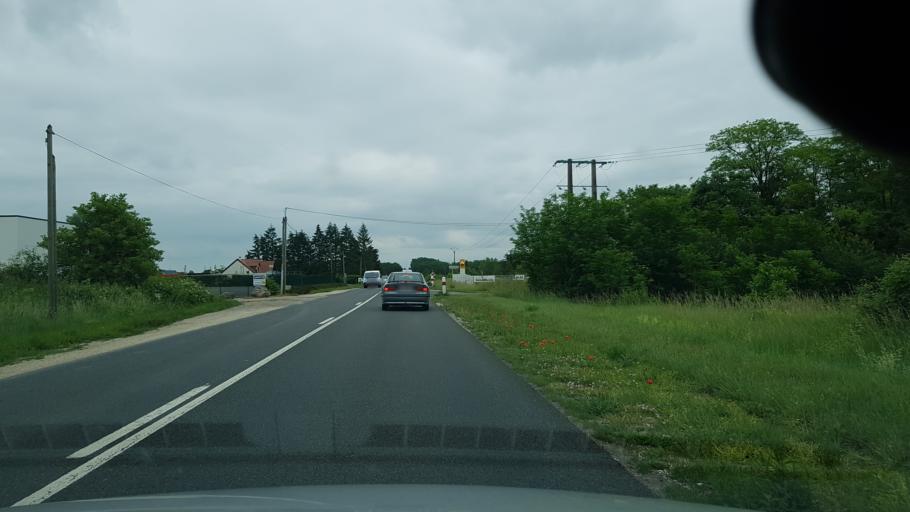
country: FR
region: Centre
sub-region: Departement du Loir-et-Cher
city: Selles-sur-Cher
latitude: 47.2930
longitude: 1.5255
